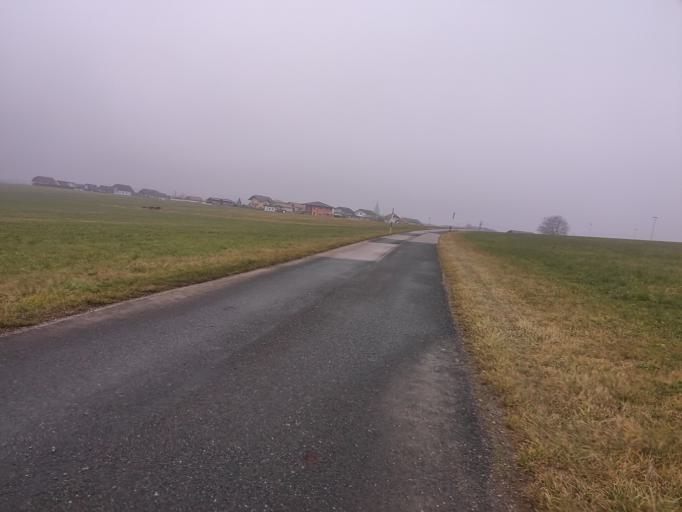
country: AT
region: Salzburg
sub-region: Politischer Bezirk Salzburg-Umgebung
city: Schleedorf
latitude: 47.9505
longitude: 13.1597
